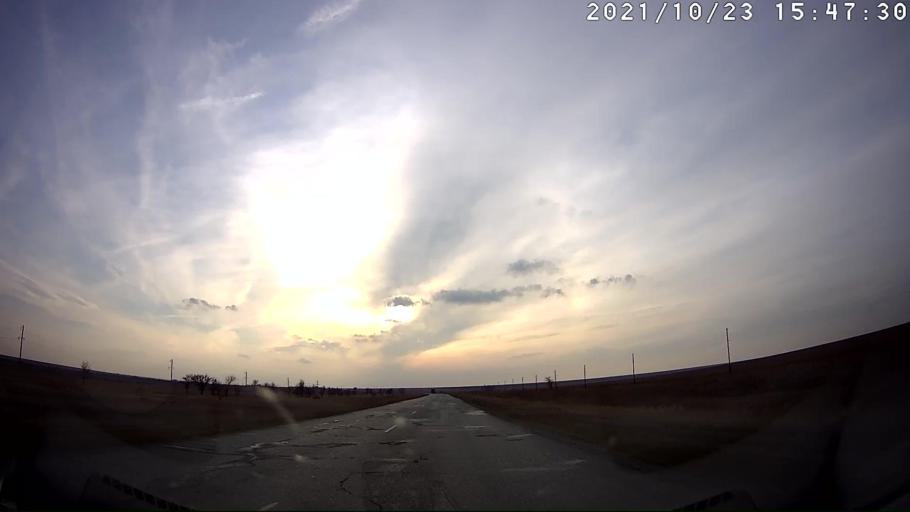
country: RU
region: Kalmykiya
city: Sadovoye
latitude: 48.0373
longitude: 44.0904
